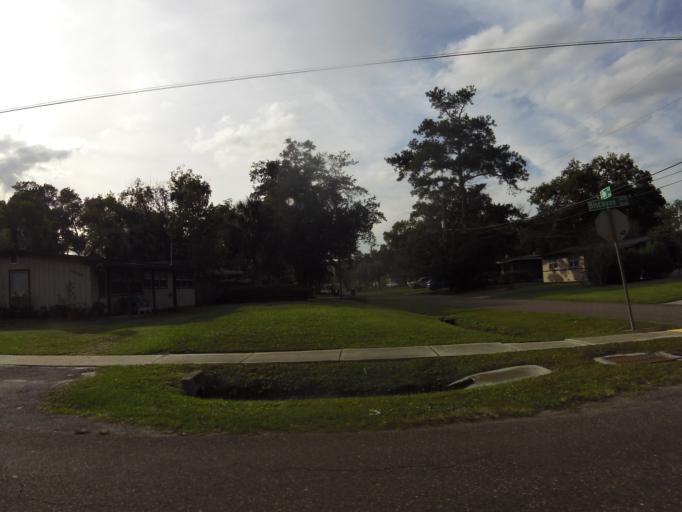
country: US
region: Florida
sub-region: Duval County
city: Jacksonville
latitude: 30.4243
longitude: -81.6746
